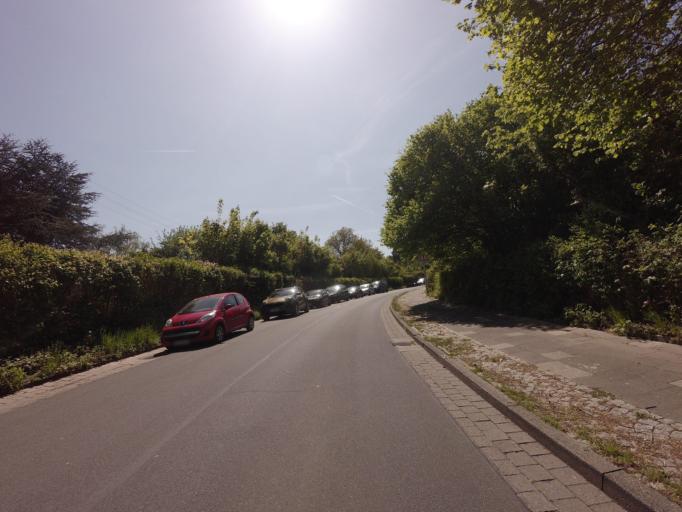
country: DE
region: Lower Saxony
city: Hildesheim
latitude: 52.1483
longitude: 9.9740
